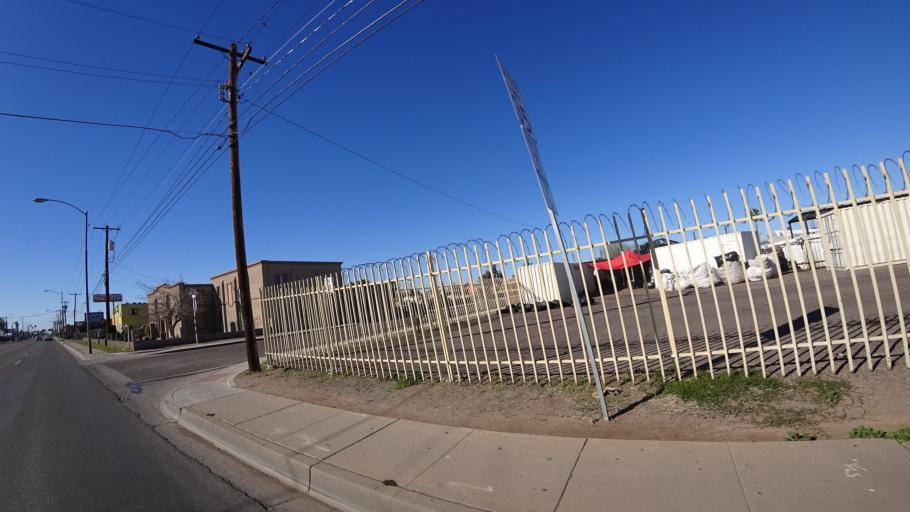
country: US
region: Arizona
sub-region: Maricopa County
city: Phoenix
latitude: 33.4368
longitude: -112.1019
